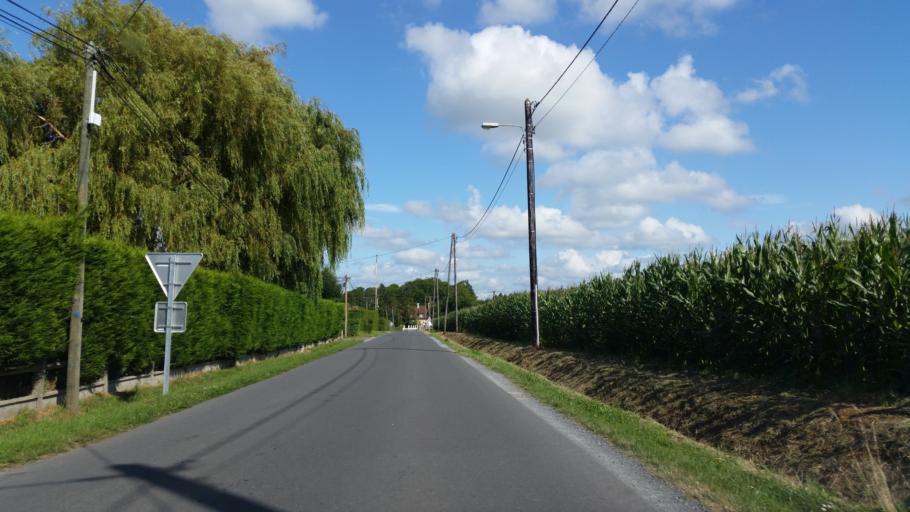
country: FR
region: Lower Normandy
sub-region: Departement du Calvados
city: Amfreville
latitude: 49.2465
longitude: -0.2106
